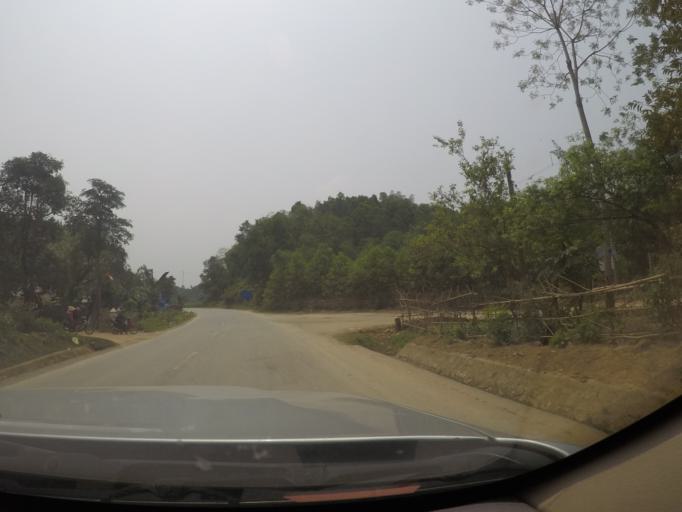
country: VN
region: Thanh Hoa
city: Thi Tran Thuong Xuan
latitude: 19.8310
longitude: 105.3899
